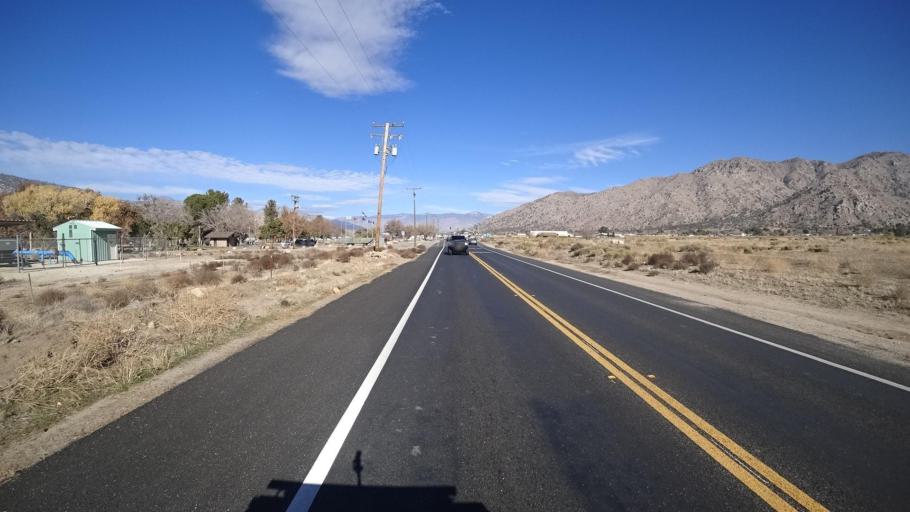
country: US
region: California
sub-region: Kern County
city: Lake Isabella
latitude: 35.6073
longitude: -118.4848
